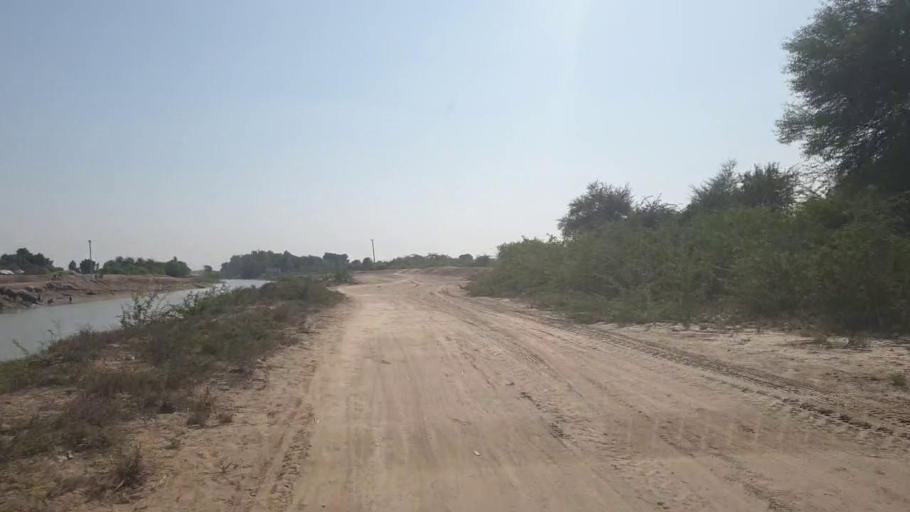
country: PK
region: Sindh
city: Tando Bago
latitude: 24.7606
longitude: 69.1543
